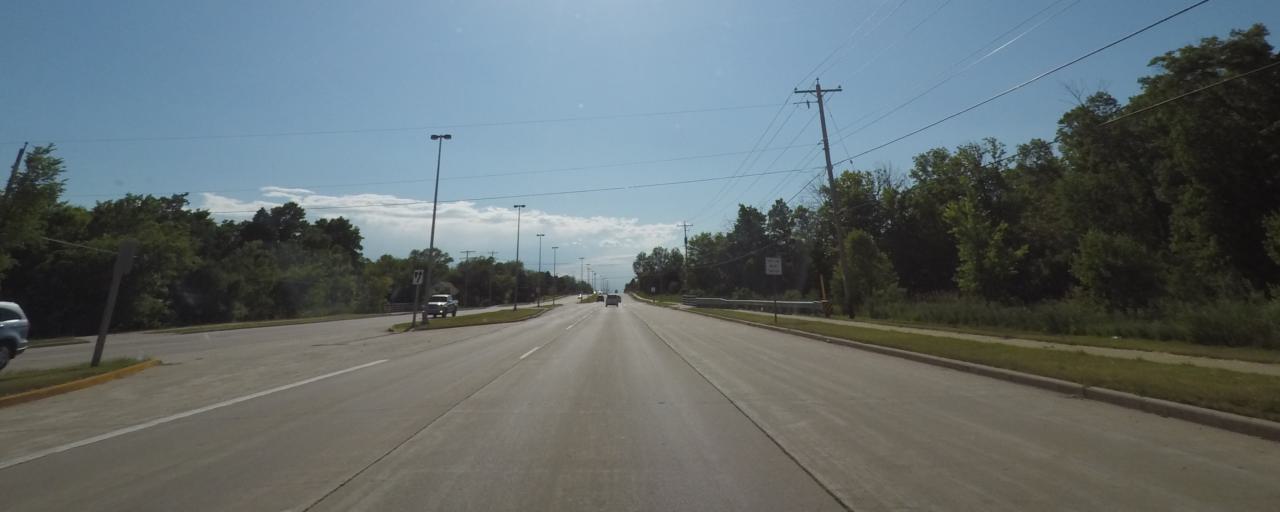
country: US
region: Wisconsin
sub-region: Milwaukee County
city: Greendale
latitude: 42.9164
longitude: -87.9579
